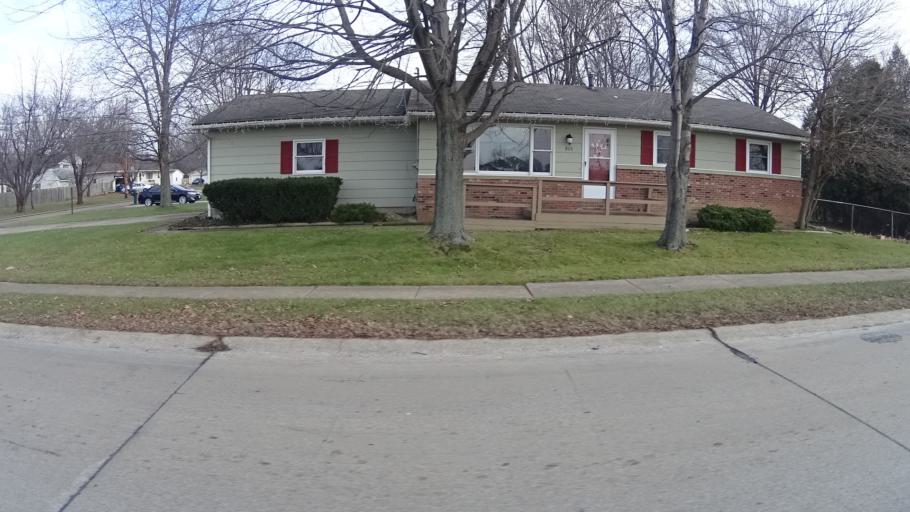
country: US
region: Ohio
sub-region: Lorain County
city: Amherst
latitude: 41.4149
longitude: -82.2177
